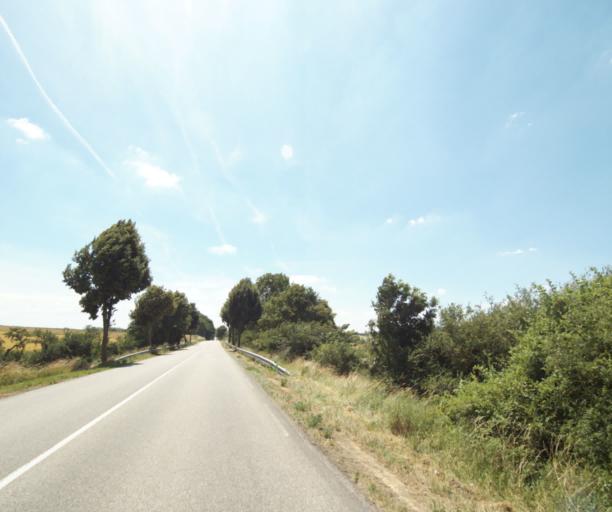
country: FR
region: Lorraine
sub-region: Departement de Meurthe-et-Moselle
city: Luneville
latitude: 48.6188
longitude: 6.4870
